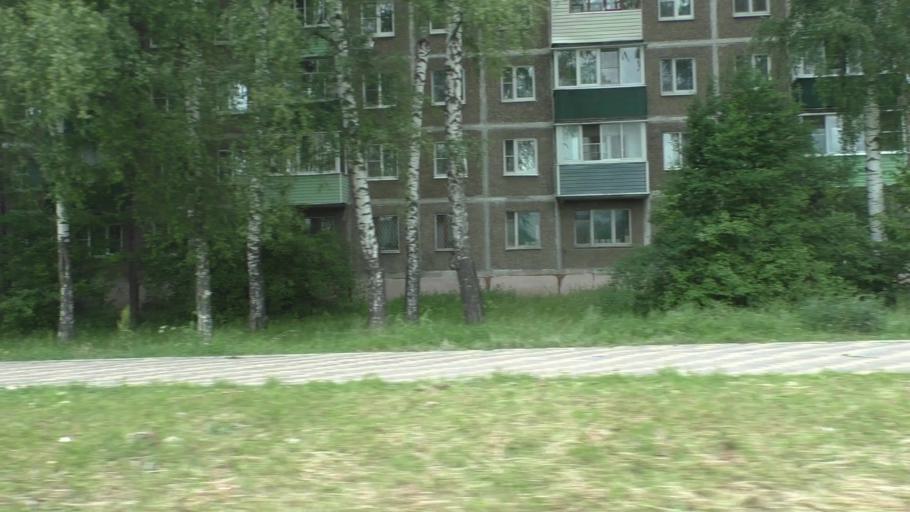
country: RU
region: Moskovskaya
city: Yegor'yevsk
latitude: 55.3648
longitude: 39.0616
